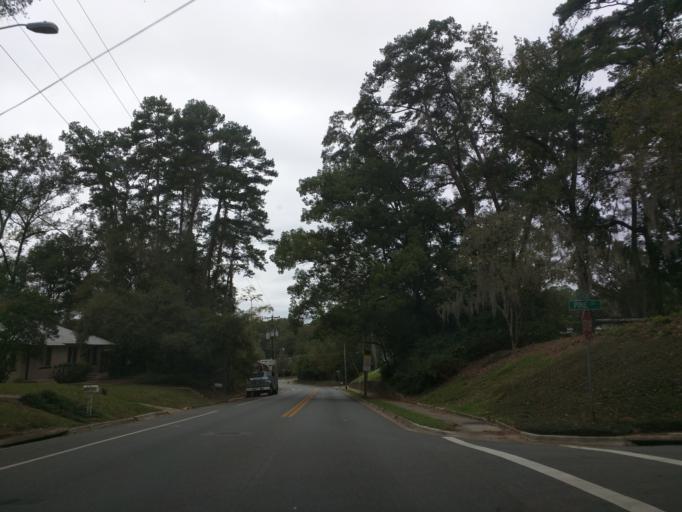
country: US
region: Florida
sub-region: Leon County
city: Tallahassee
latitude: 30.4512
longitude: -84.2714
